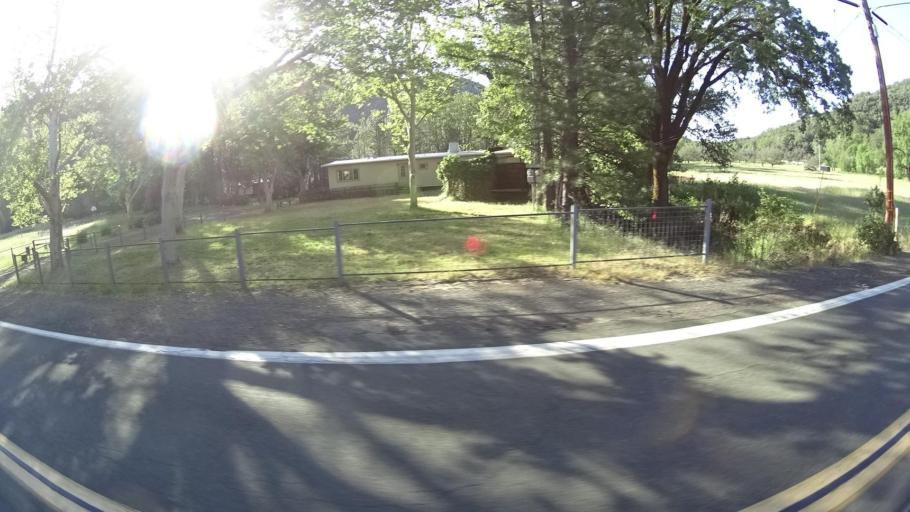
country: US
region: California
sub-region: Lake County
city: Upper Lake
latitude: 39.1428
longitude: -123.0029
